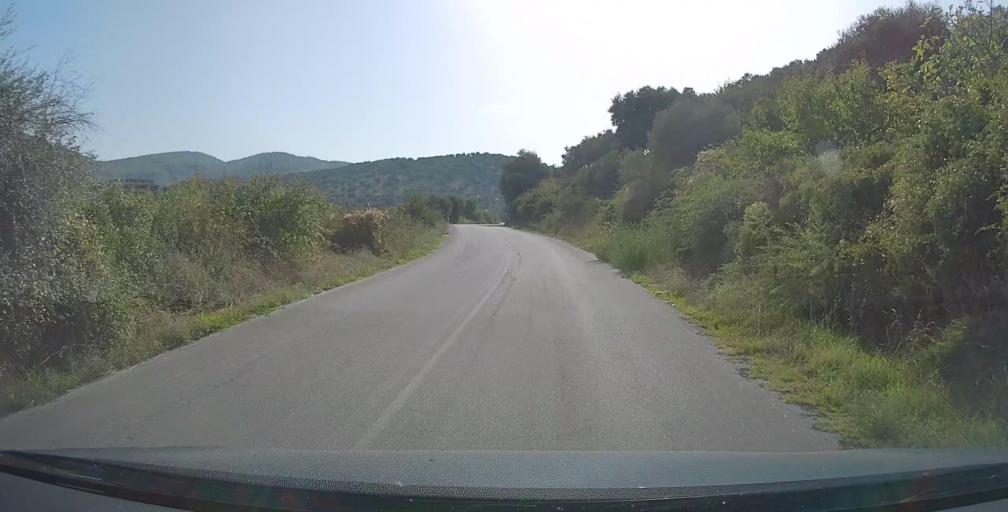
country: GR
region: Central Macedonia
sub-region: Nomos Chalkidikis
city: Sykia
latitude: 39.9764
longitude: 23.9069
